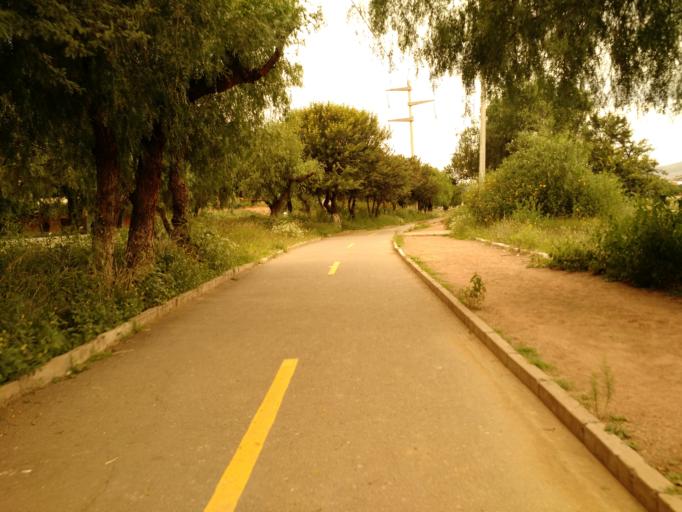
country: BO
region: Cochabamba
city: Cochabamba
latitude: -17.4124
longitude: -66.1266
